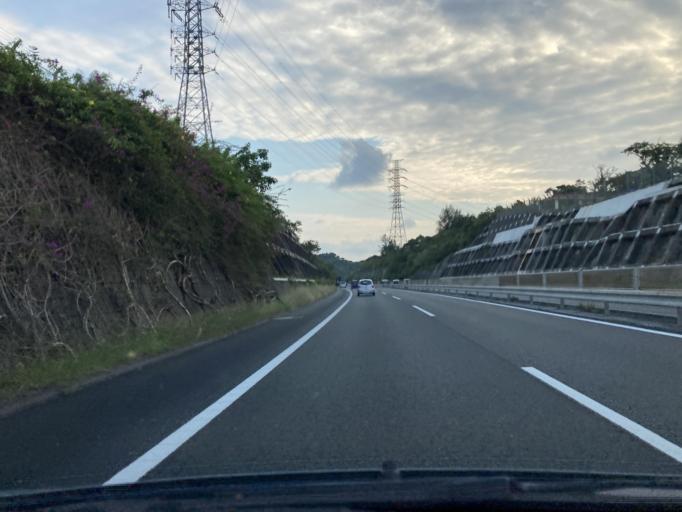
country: JP
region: Okinawa
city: Chatan
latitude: 26.3149
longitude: 127.7885
